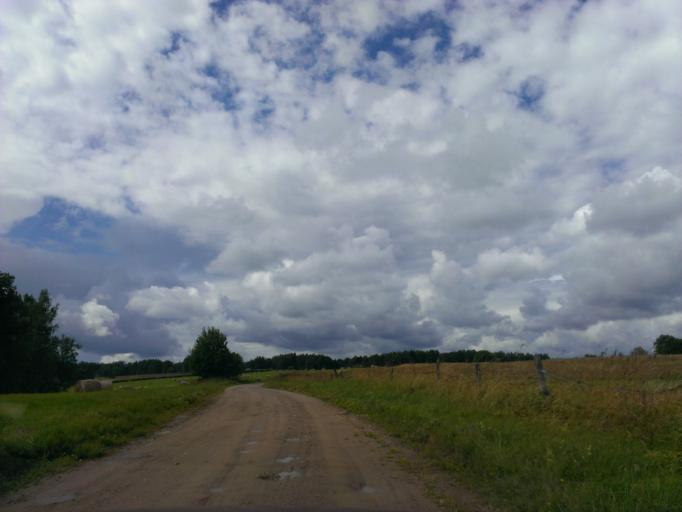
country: LV
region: Ligatne
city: Ligatne
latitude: 57.2256
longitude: 24.9997
